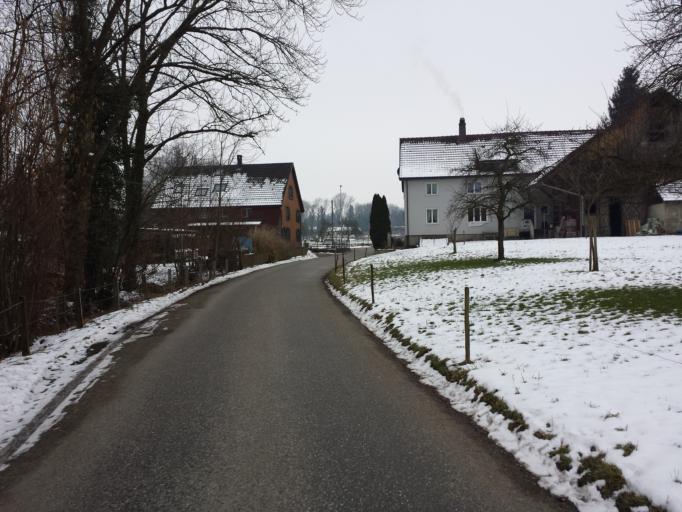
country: CH
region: Thurgau
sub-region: Arbon District
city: Egnach
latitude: 47.5380
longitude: 9.3654
